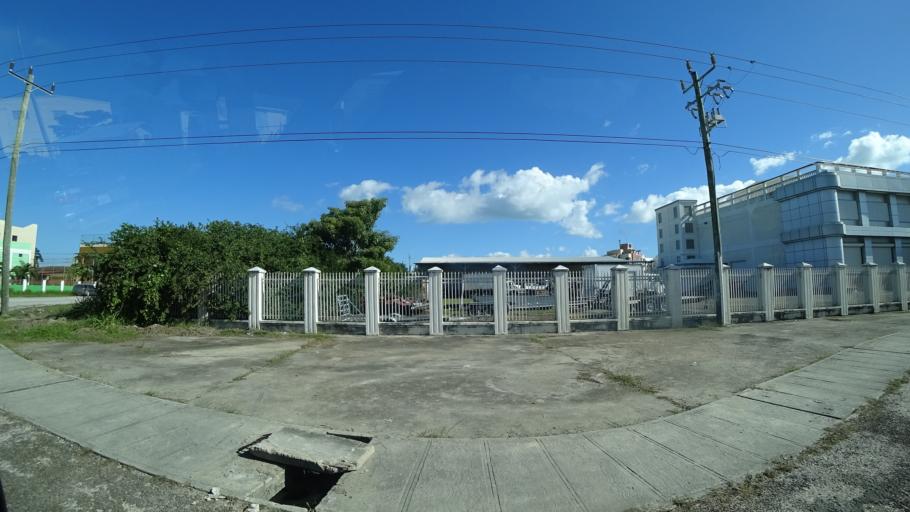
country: BZ
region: Belize
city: Belize City
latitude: 17.5066
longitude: -88.2025
